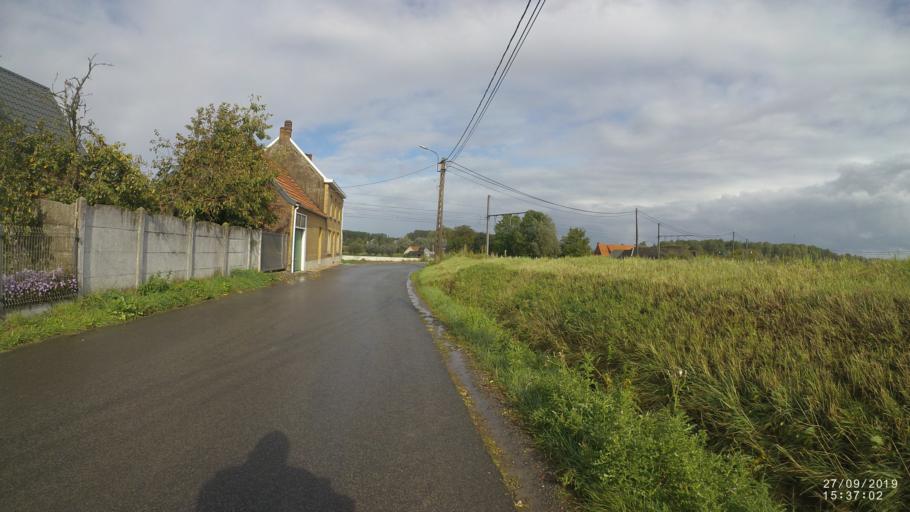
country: BE
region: Flanders
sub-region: Provincie Oost-Vlaanderen
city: Zottegem
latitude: 50.8737
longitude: 3.7437
